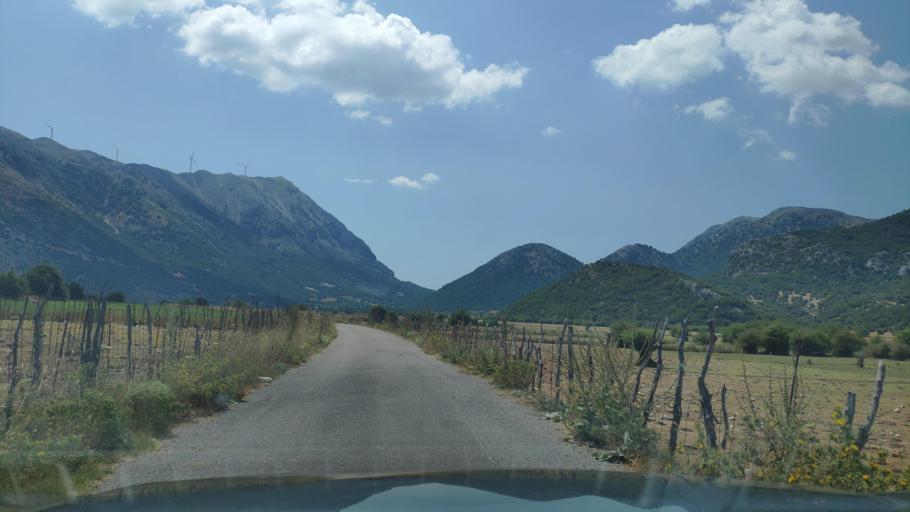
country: GR
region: West Greece
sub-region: Nomos Aitolias kai Akarnanias
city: Monastirakion
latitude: 38.7911
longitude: 20.9612
